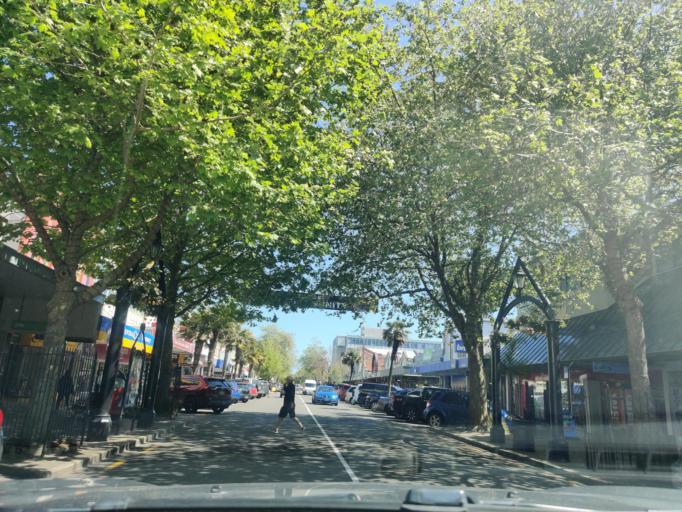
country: NZ
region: Manawatu-Wanganui
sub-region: Wanganui District
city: Wanganui
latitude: -39.9325
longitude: 175.0512
